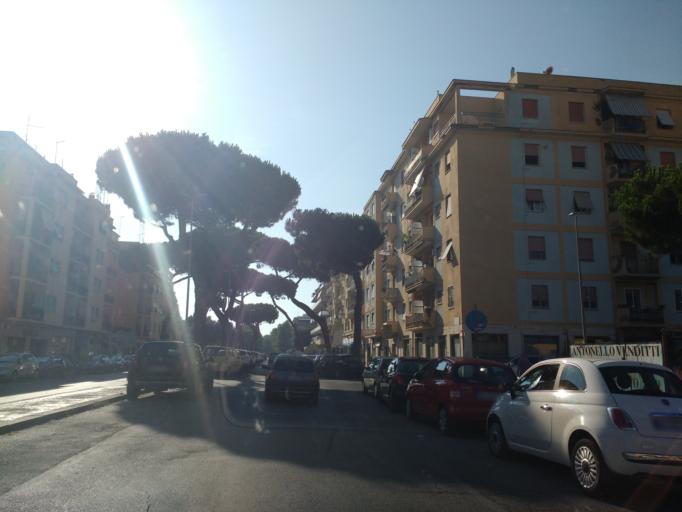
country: IT
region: Latium
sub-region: Citta metropolitana di Roma Capitale
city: Lido di Ostia
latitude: 41.7312
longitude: 12.2853
